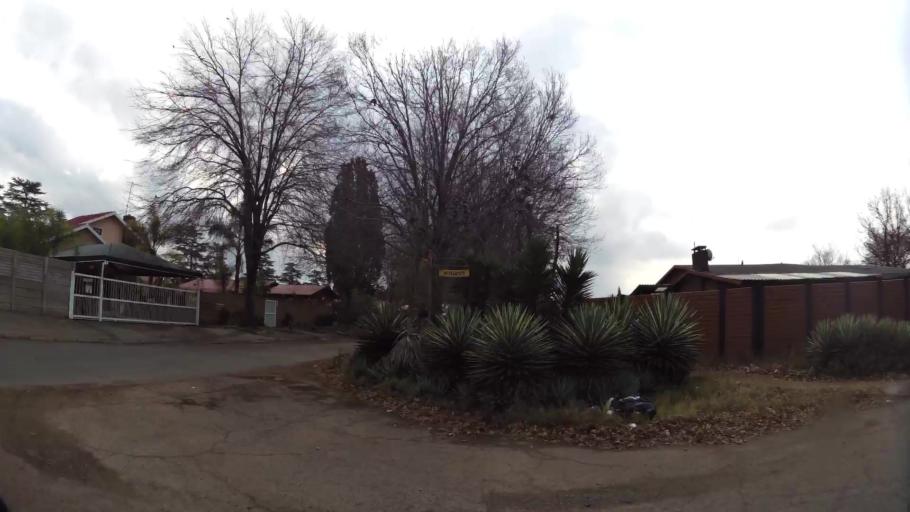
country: ZA
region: Gauteng
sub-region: Sedibeng District Municipality
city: Vanderbijlpark
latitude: -26.7114
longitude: 27.8369
